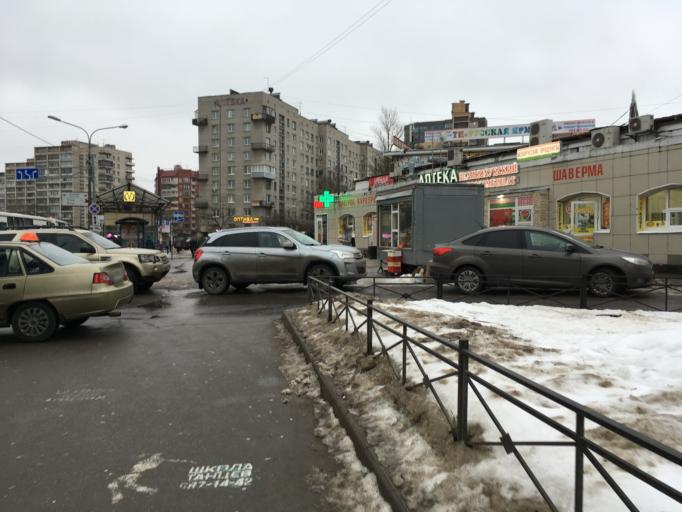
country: RU
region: St.-Petersburg
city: Dachnoye
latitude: 59.8416
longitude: 30.2528
